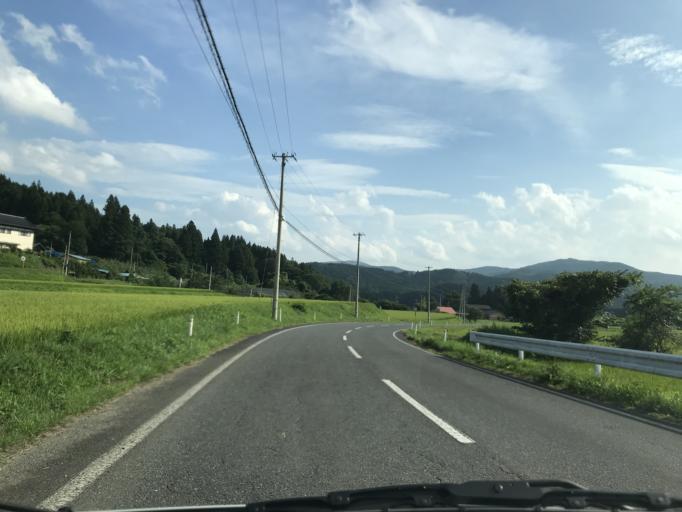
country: JP
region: Iwate
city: Ofunato
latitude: 38.9479
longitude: 141.4622
